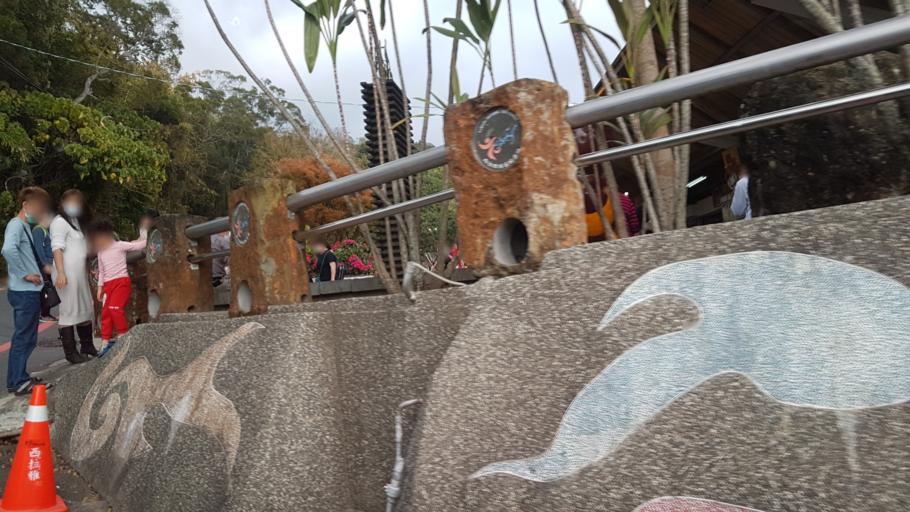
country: TW
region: Taiwan
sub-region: Chiayi
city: Jiayi Shi
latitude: 23.3216
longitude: 120.4835
